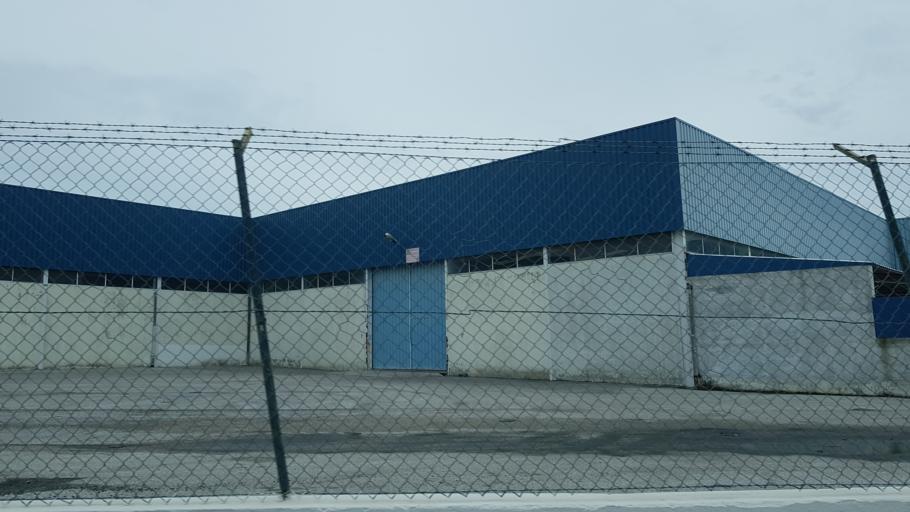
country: PT
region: Lisbon
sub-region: Alenquer
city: Carregado
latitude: 39.0335
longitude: -8.9638
